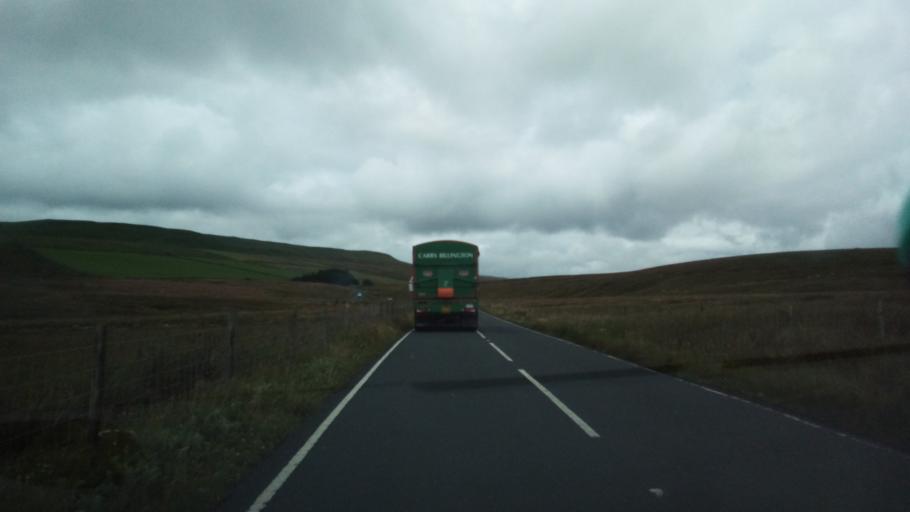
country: GB
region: England
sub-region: North Yorkshire
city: Ingleton
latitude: 54.2452
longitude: -2.3162
